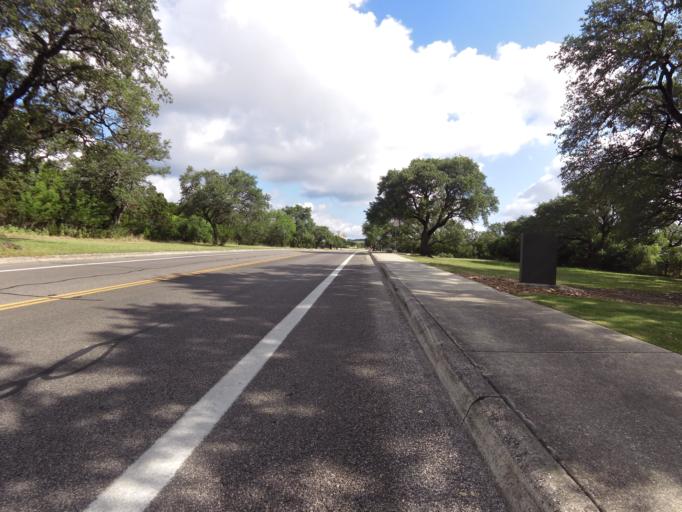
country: US
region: Texas
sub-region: Bexar County
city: Shavano Park
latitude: 29.5873
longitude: -98.6074
